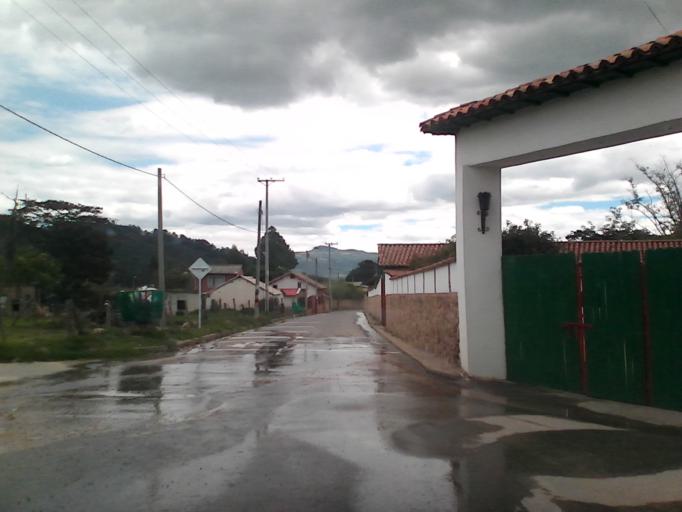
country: CO
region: Boyaca
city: Duitama
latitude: 5.8203
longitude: -73.0712
